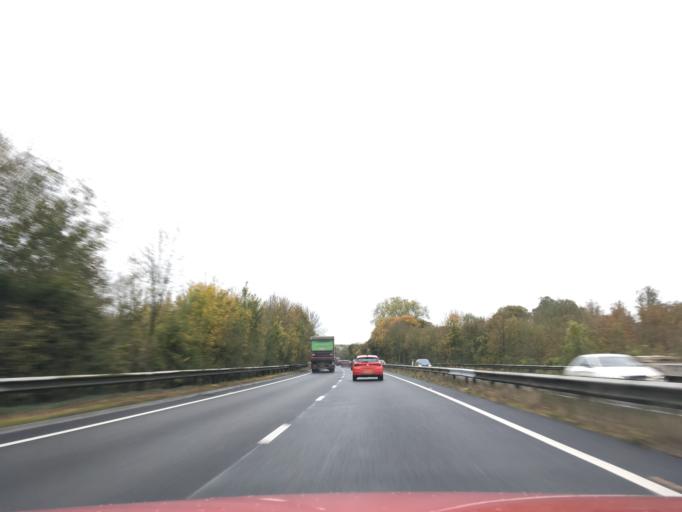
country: GB
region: England
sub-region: Hampshire
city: Overton
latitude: 51.2294
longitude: -1.3481
